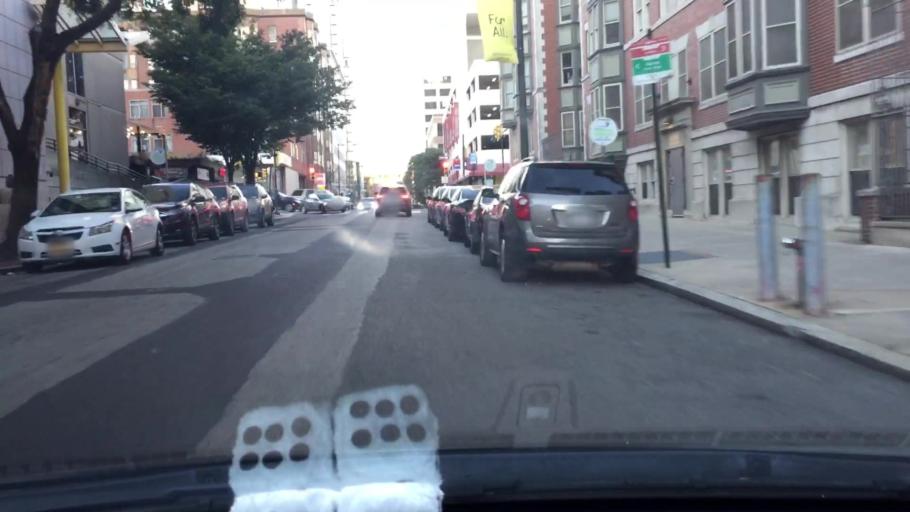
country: US
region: Pennsylvania
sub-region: Philadelphia County
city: Philadelphia
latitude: 39.9540
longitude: -75.1946
